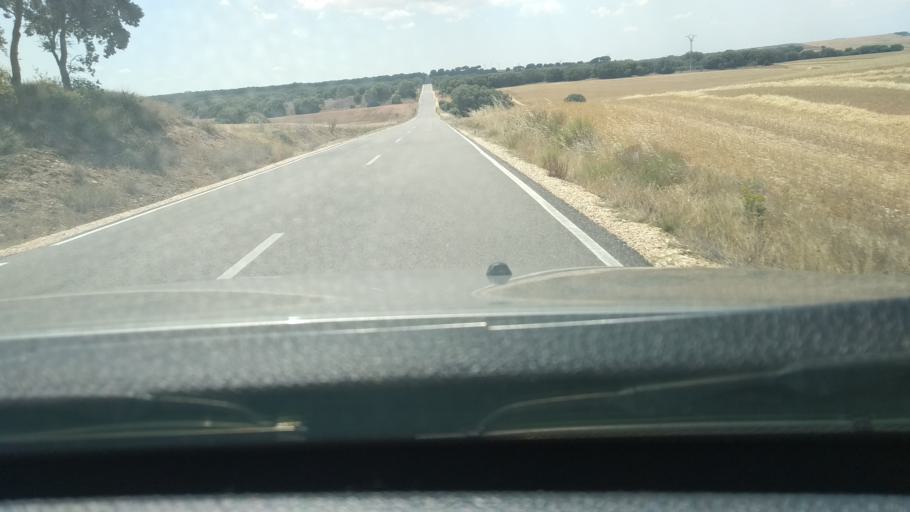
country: ES
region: Castille and Leon
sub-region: Provincia de Burgos
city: Avellanosa de Muno
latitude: 41.9724
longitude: -3.8100
